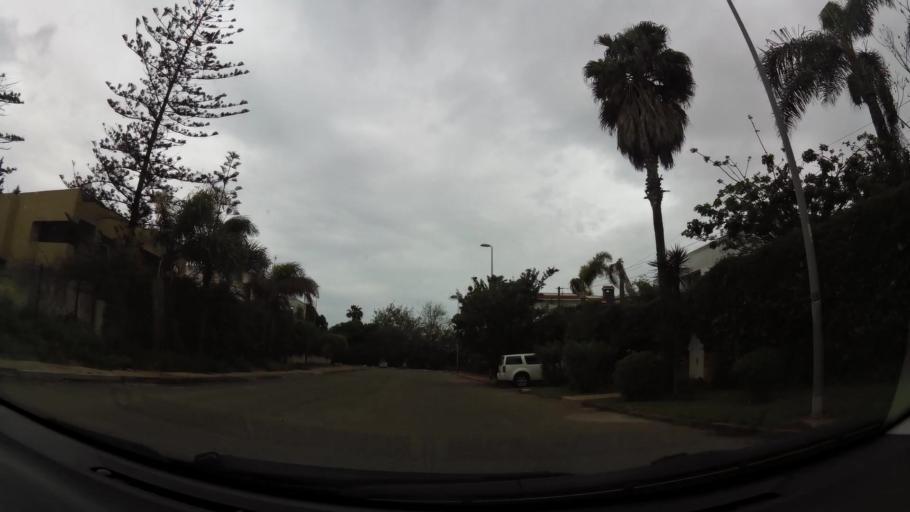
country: MA
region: Grand Casablanca
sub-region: Casablanca
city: Casablanca
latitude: 33.5772
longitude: -7.6665
